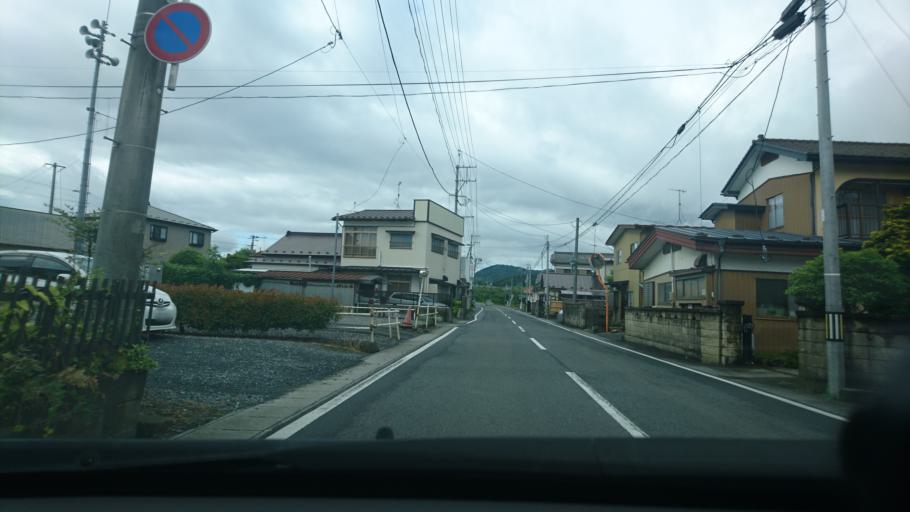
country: JP
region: Miyagi
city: Wakuya
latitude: 38.6067
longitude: 141.3010
